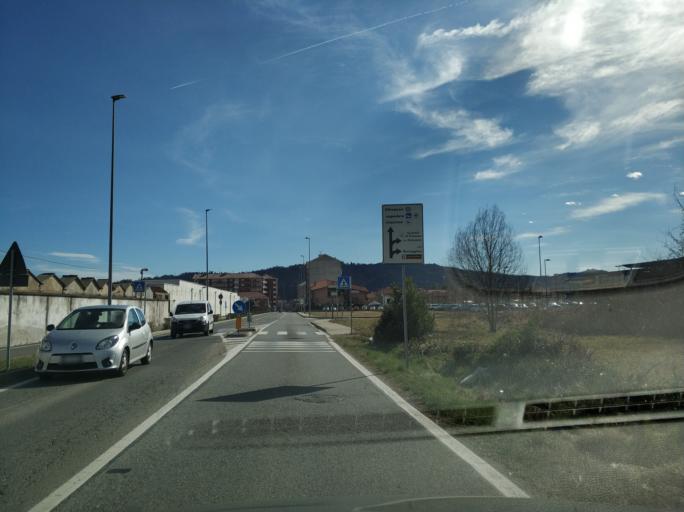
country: IT
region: Piedmont
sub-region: Provincia di Torino
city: Chivasso
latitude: 45.1991
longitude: 7.8899
